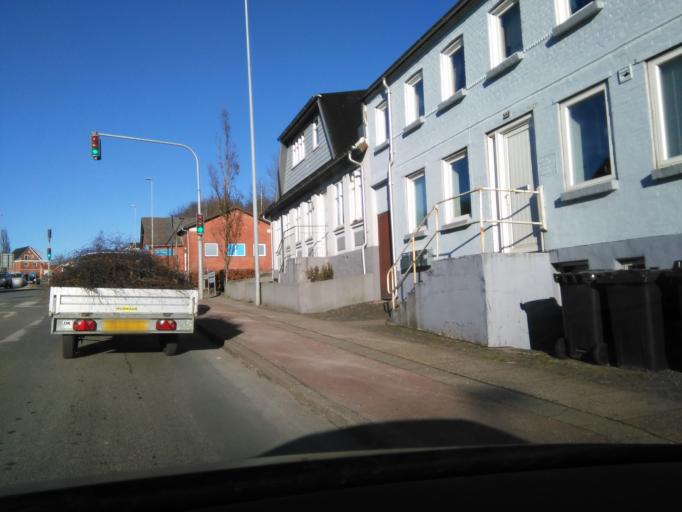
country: DK
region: North Denmark
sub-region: Mariagerfjord Kommune
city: Hobro
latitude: 56.6426
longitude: 9.7929
